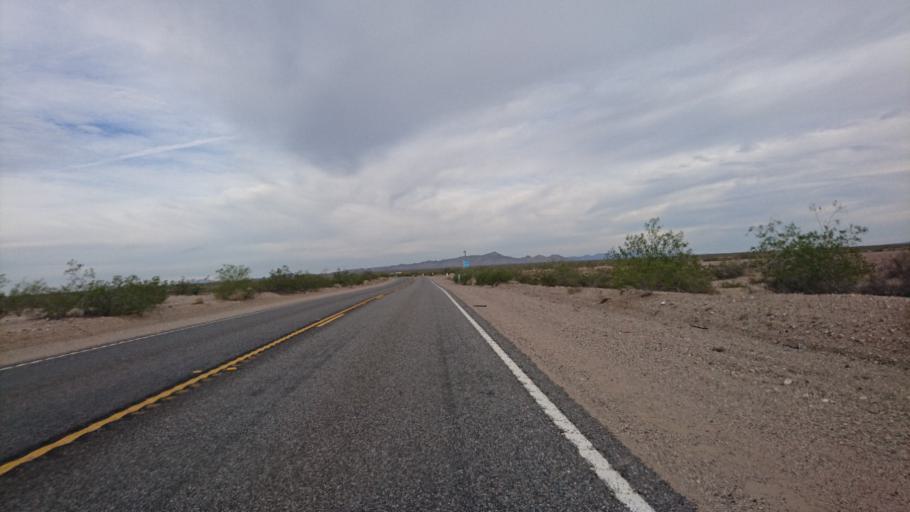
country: US
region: Arizona
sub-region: Mohave County
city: Willow Valley
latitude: 34.9375
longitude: -114.8084
